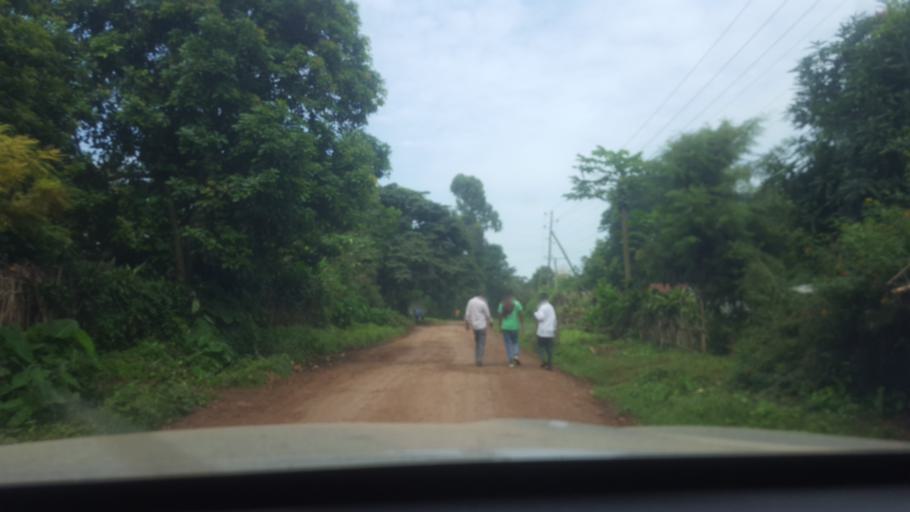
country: ET
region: Southern Nations, Nationalities, and People's Region
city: Tippi
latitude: 7.2448
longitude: 35.3384
